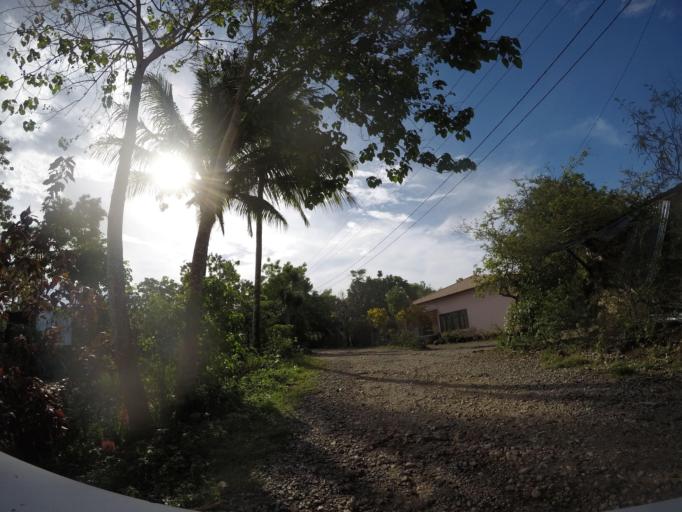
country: TL
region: Baucau
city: Baucau
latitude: -8.5082
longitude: 126.4457
